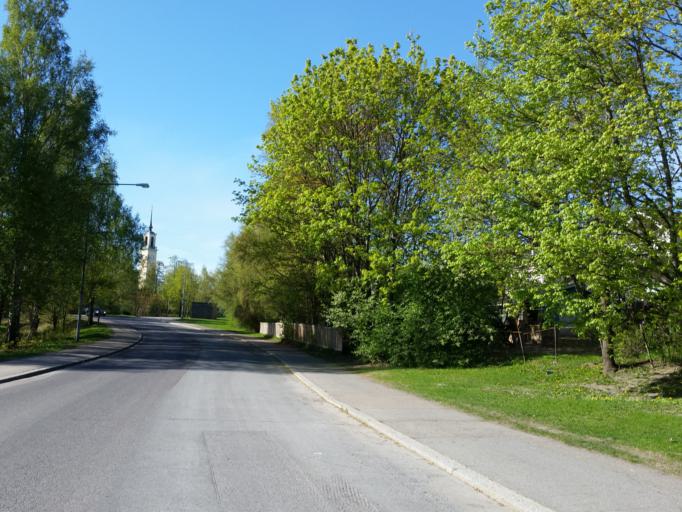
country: FI
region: Pirkanmaa
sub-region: Tampere
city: Tampere
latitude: 61.4897
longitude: 23.7859
